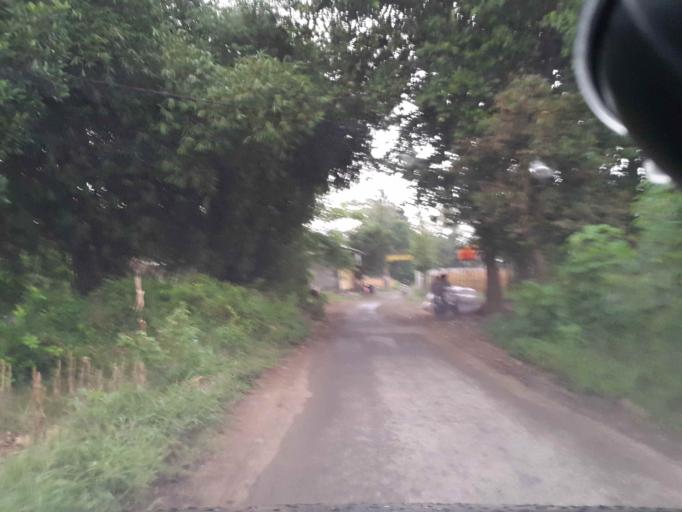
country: ID
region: West Nusa Tenggara
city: Karangkebon Timur
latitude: -8.6587
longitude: 116.1145
